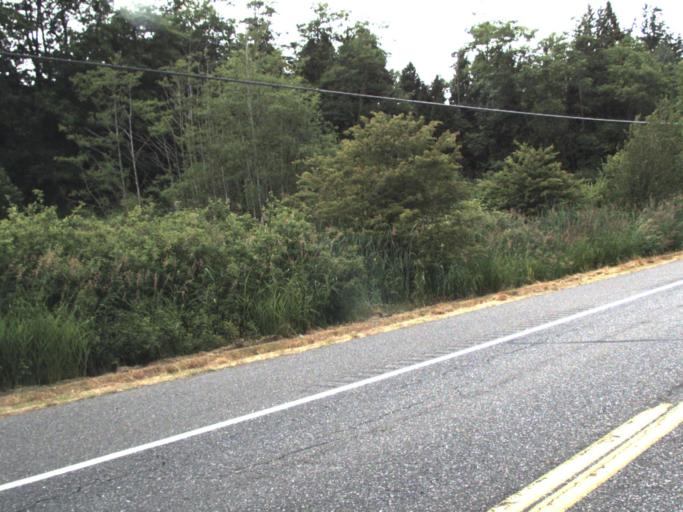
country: US
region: Washington
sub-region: Whatcom County
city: Birch Bay
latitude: 48.8921
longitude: -122.6806
